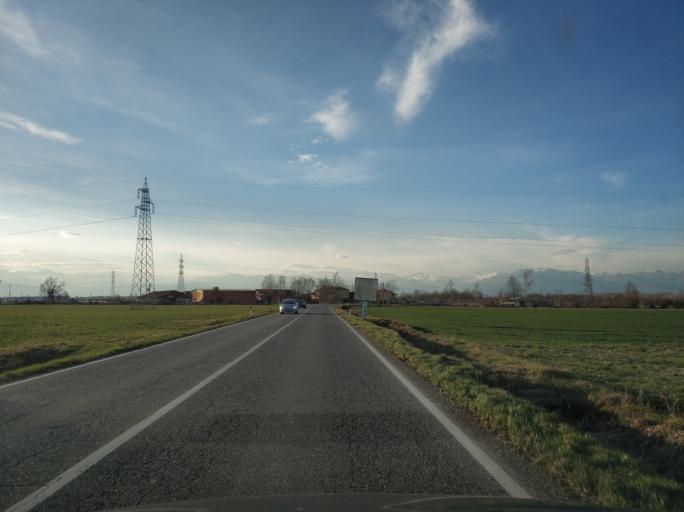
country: IT
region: Piedmont
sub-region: Provincia di Torino
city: Brandizzo
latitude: 45.1848
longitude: 7.8273
